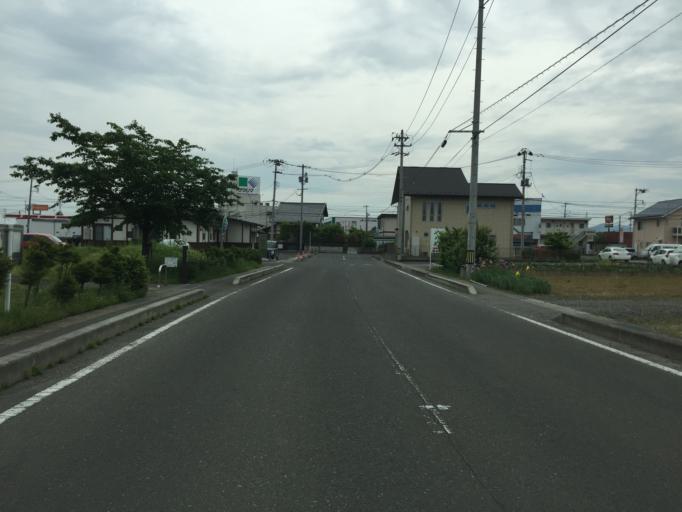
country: JP
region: Fukushima
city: Fukushima-shi
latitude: 37.7927
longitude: 140.4583
